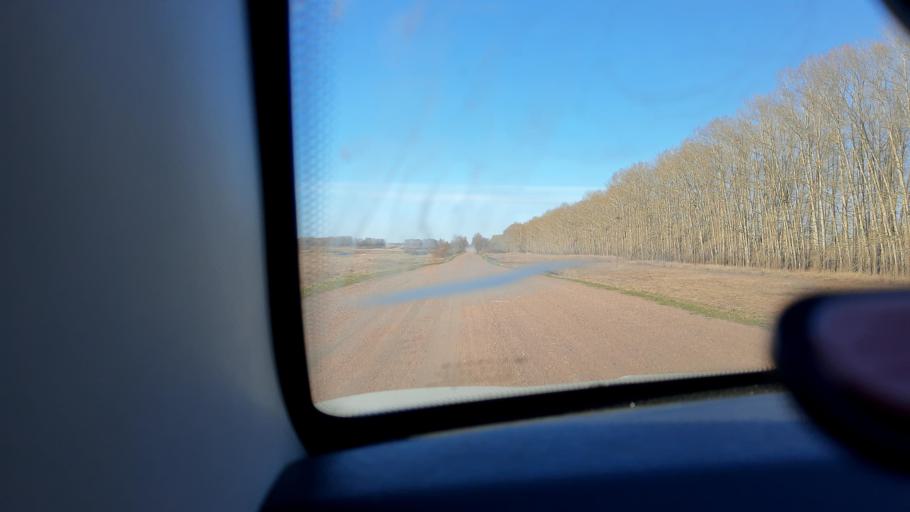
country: RU
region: Bashkortostan
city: Asanovo
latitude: 54.8555
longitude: 55.4586
